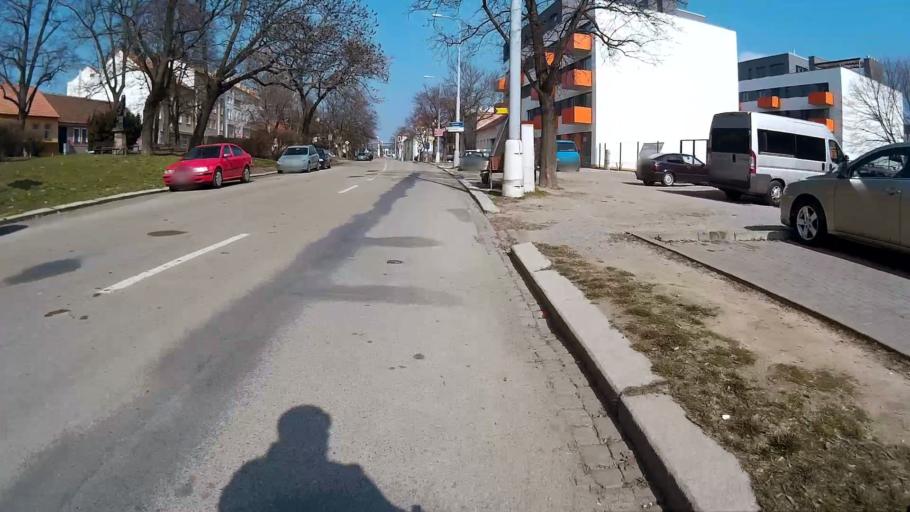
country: CZ
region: South Moravian
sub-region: Mesto Brno
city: Brno
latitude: 49.2245
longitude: 16.5973
